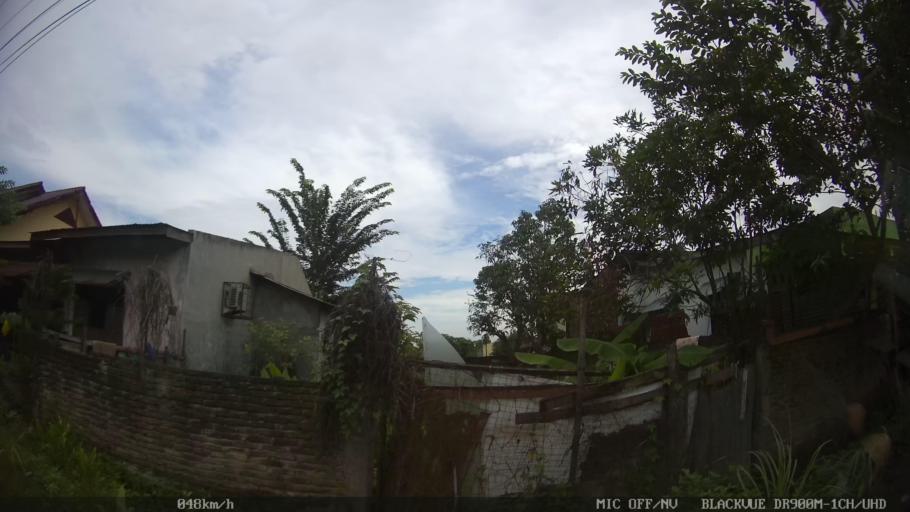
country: ID
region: North Sumatra
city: Sunggal
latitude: 3.6140
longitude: 98.5989
